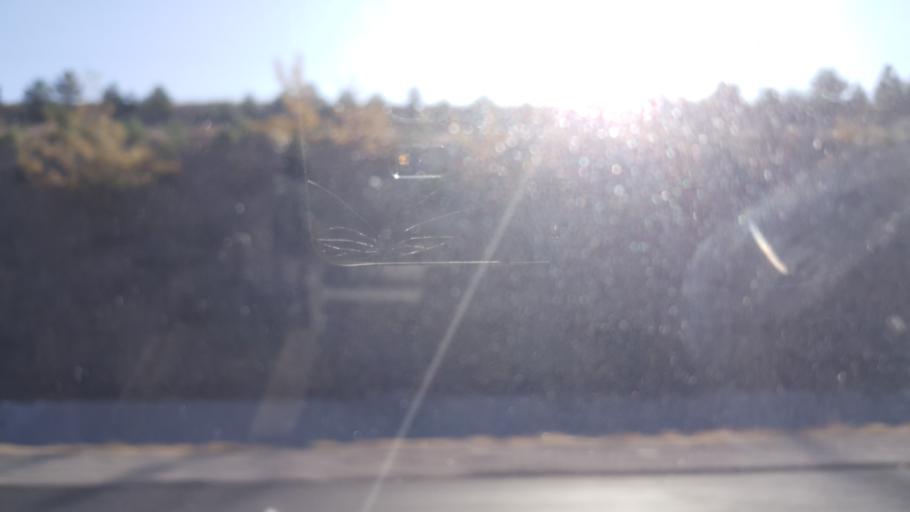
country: TR
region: Ankara
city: Cankaya
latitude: 39.8370
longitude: 32.8909
